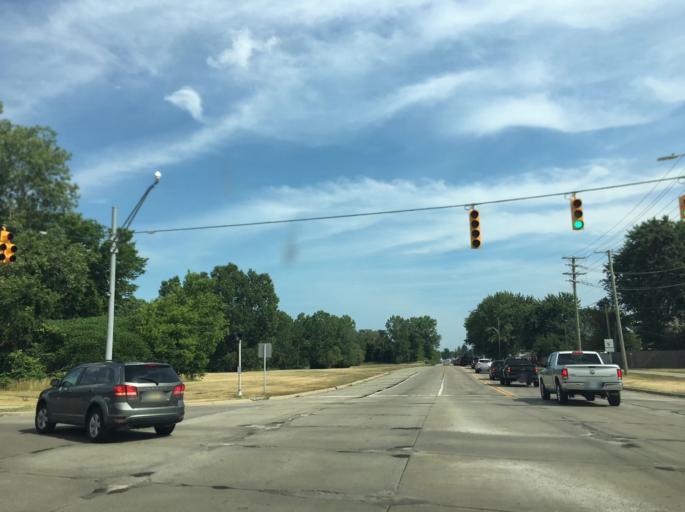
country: US
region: Michigan
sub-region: Macomb County
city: Sterling Heights
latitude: 42.5818
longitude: -82.9956
